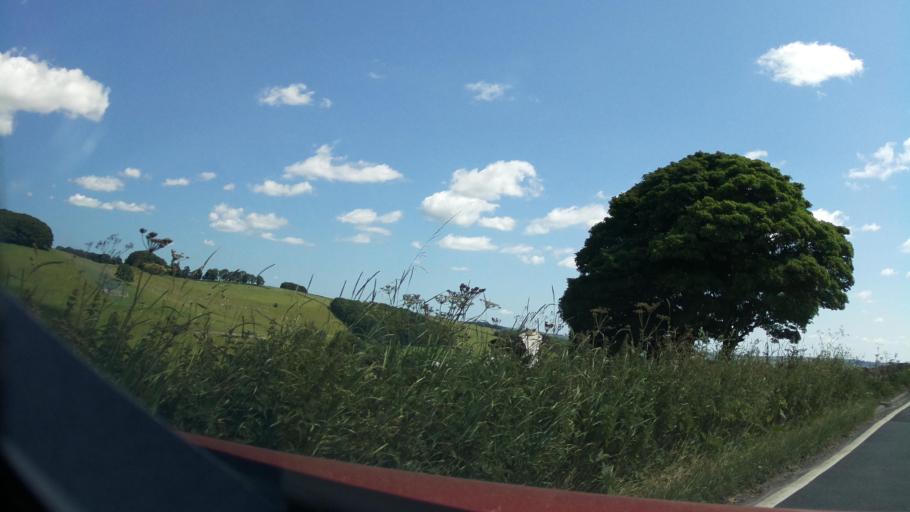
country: GB
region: England
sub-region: Derbyshire
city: Ashbourne
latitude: 53.0937
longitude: -1.7714
